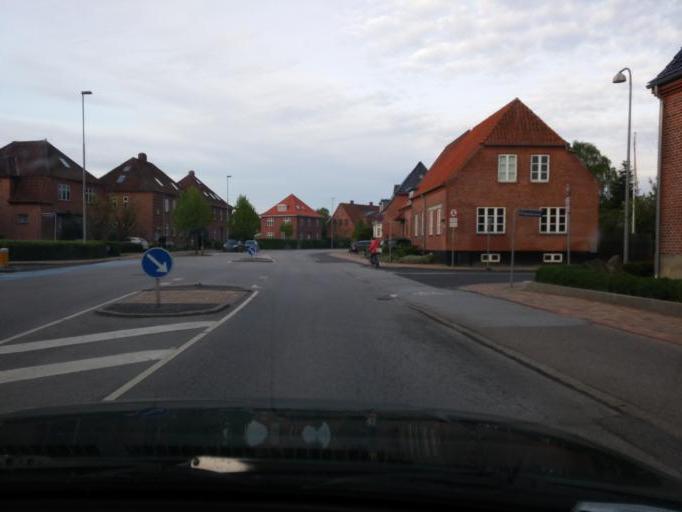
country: DK
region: South Denmark
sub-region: Odense Kommune
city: Odense
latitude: 55.3915
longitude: 10.4016
